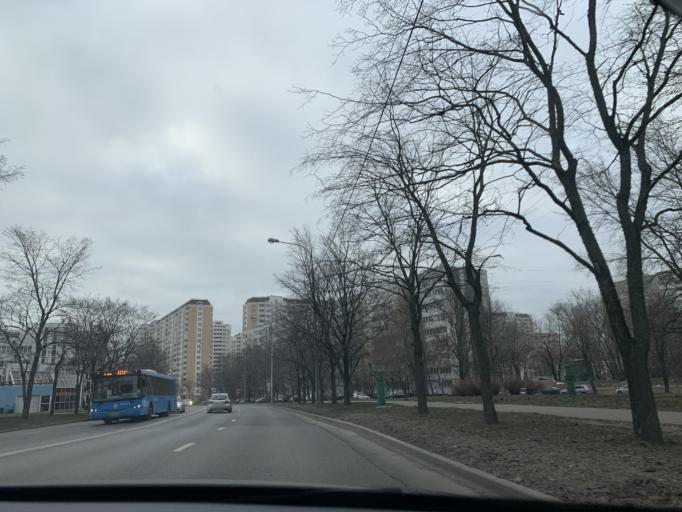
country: RU
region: Moskovskaya
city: Vostochnoe Degunino
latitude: 55.8760
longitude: 37.5576
